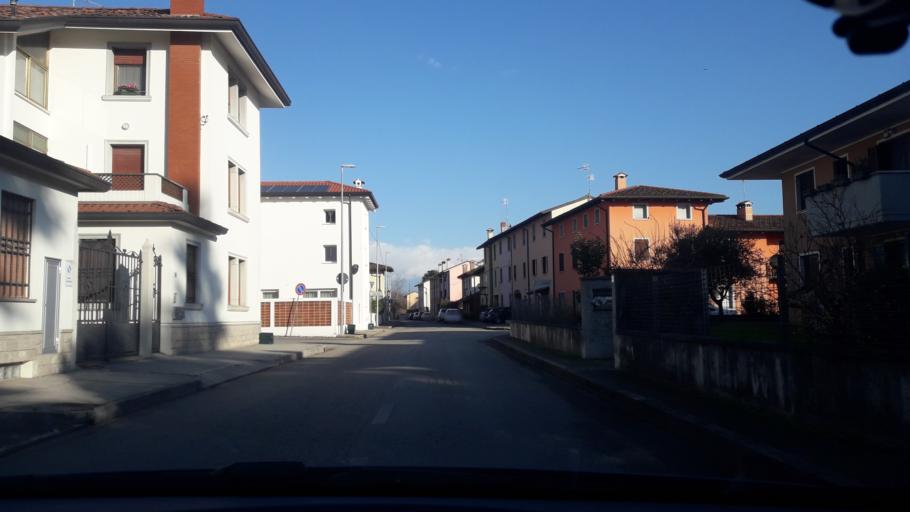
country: IT
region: Friuli Venezia Giulia
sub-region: Provincia di Udine
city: Passons
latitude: 46.0698
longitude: 13.1914
